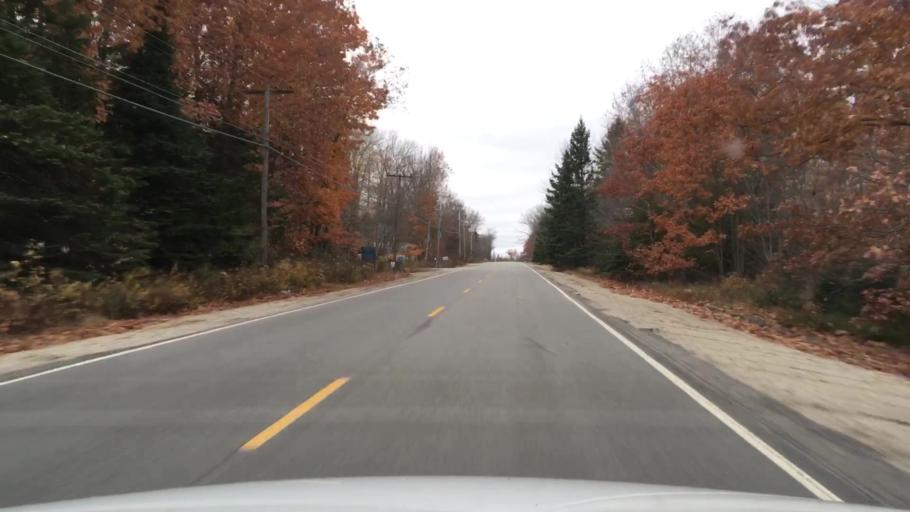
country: US
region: Maine
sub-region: Hancock County
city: Sedgwick
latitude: 44.3980
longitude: -68.5883
